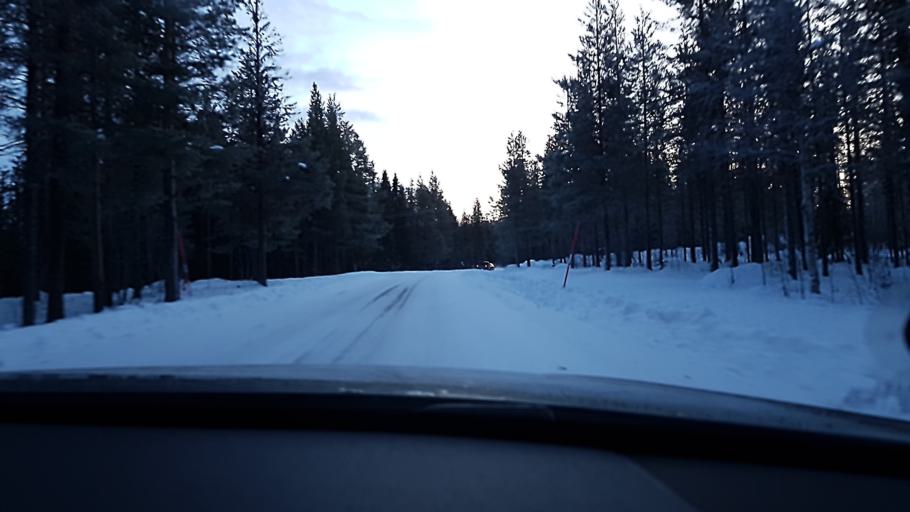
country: SE
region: Vaesterbotten
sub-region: Sorsele Kommun
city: Sorsele
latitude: 65.4984
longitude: 17.5567
